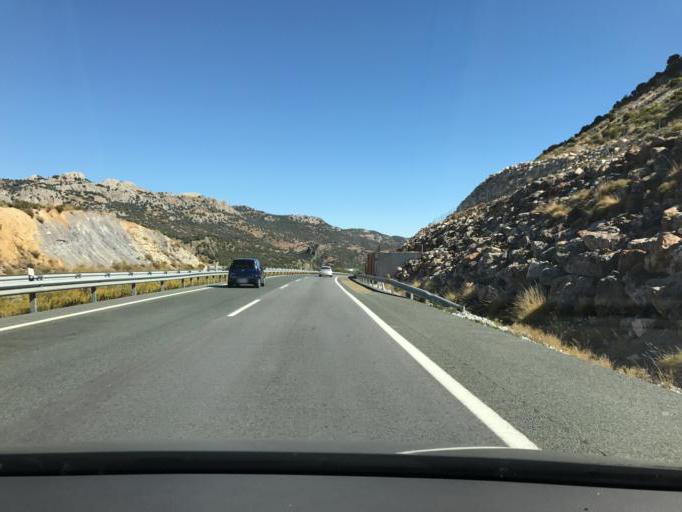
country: ES
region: Andalusia
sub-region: Provincia de Granada
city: Beas de Granada
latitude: 37.3000
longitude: -3.4321
